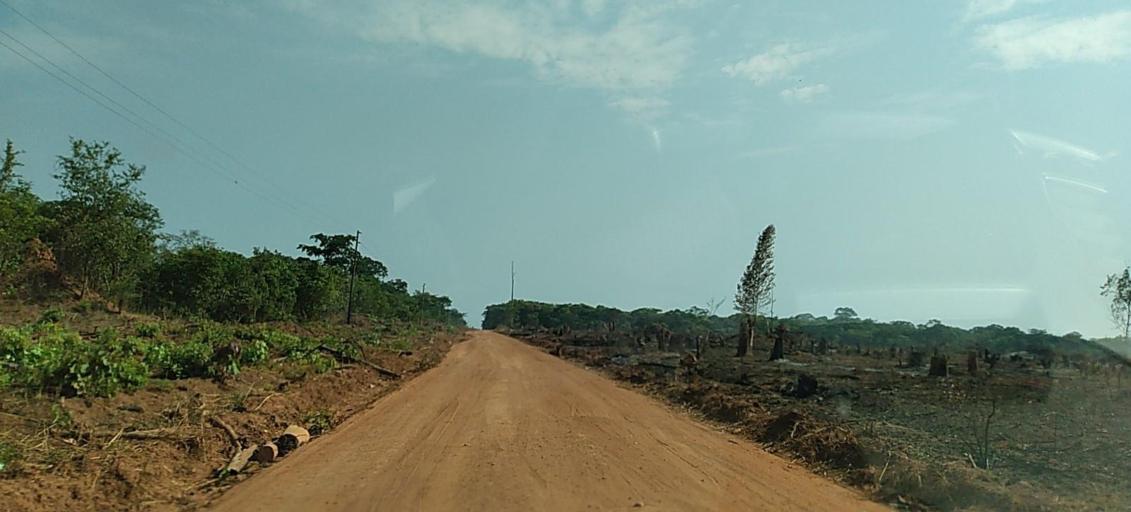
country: ZM
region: Copperbelt
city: Kalulushi
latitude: -12.9941
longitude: 27.8145
